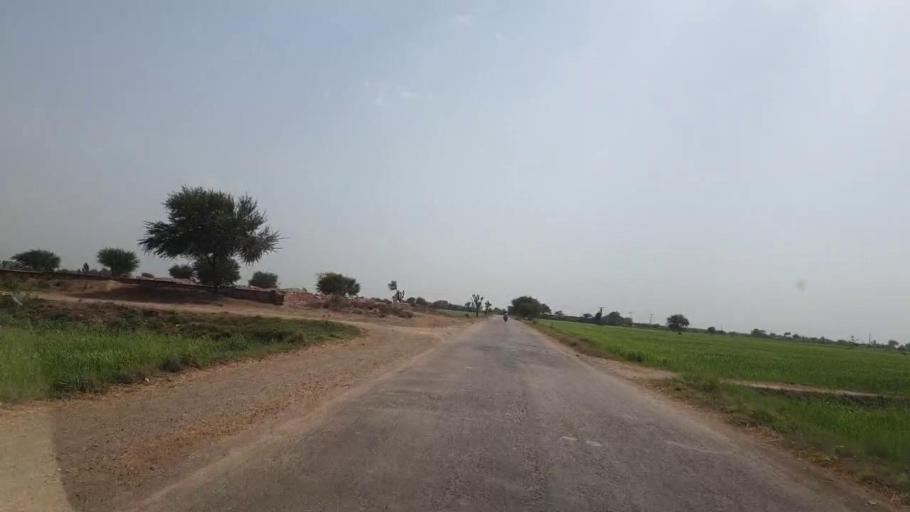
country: PK
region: Sindh
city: Tando Ghulam Ali
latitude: 25.0694
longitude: 68.8230
